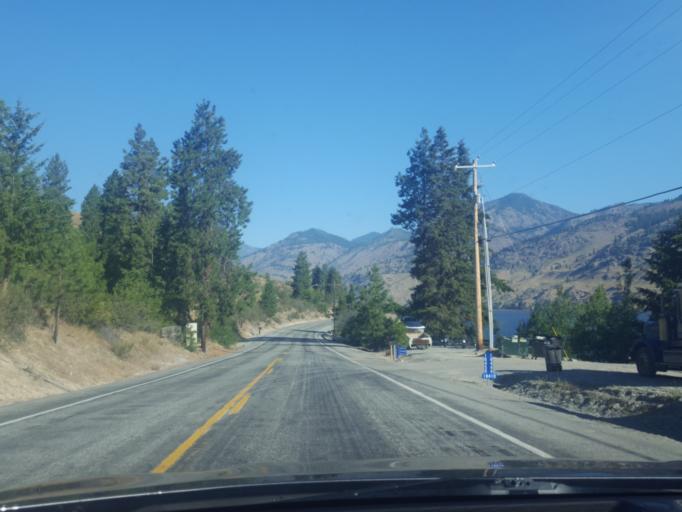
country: US
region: Washington
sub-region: Chelan County
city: Granite Falls
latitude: 47.9831
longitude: -120.2305
